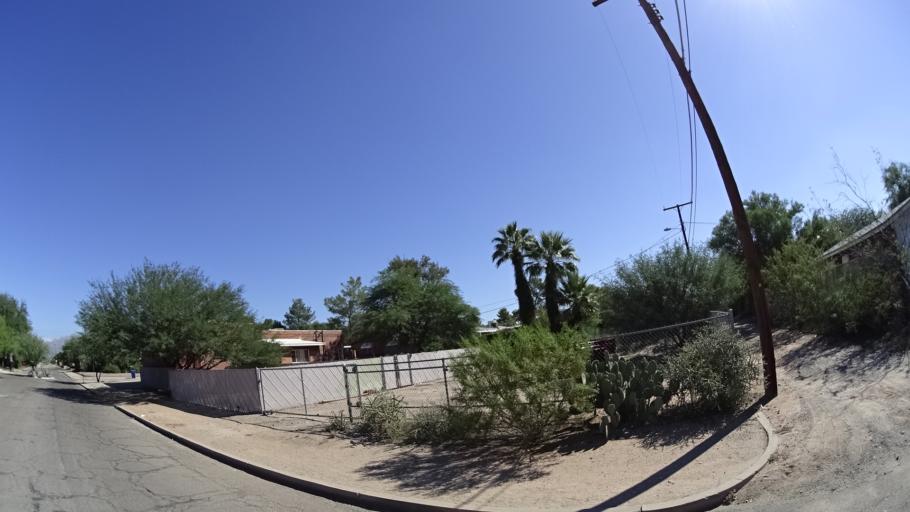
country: US
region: Arizona
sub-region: Pima County
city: Tucson
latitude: 32.2483
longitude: -110.9498
